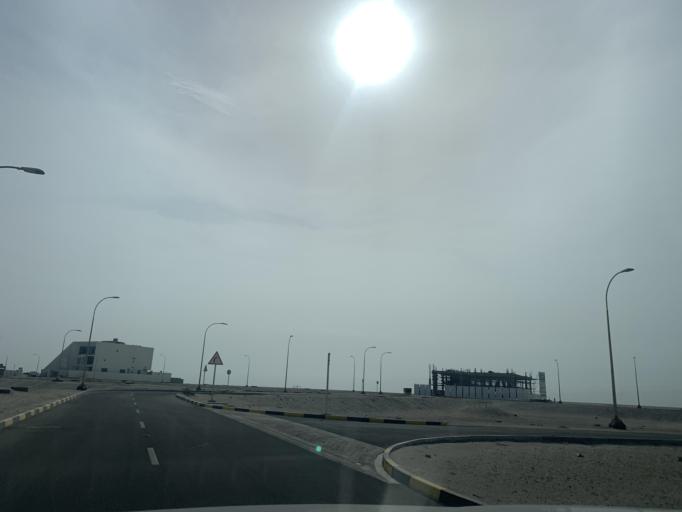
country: BH
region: Muharraq
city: Al Muharraq
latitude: 26.3192
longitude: 50.6231
